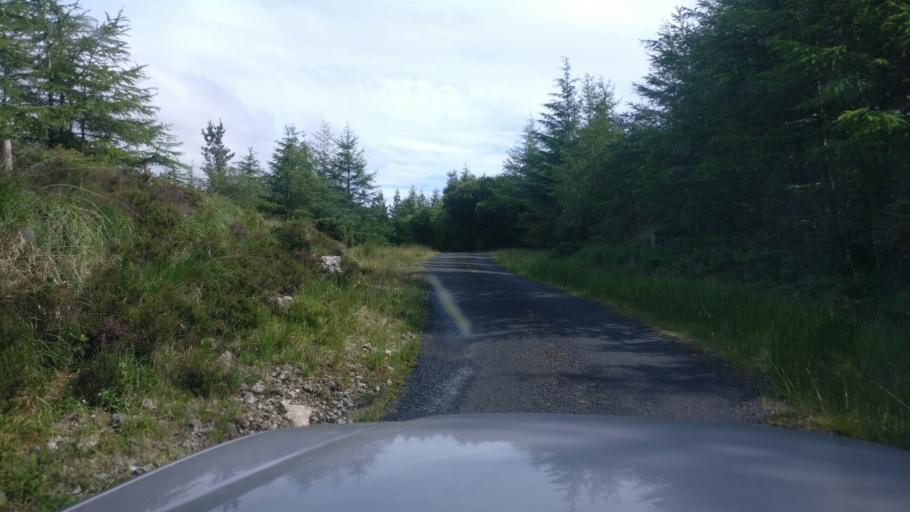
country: IE
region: Connaught
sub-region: County Galway
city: Gort
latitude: 53.0847
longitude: -8.6928
